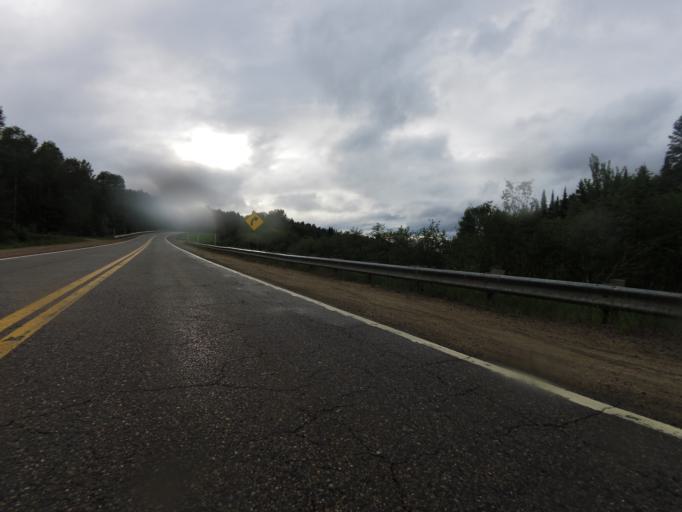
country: CA
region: Quebec
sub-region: Outaouais
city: Shawville
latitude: 45.9054
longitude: -76.2750
